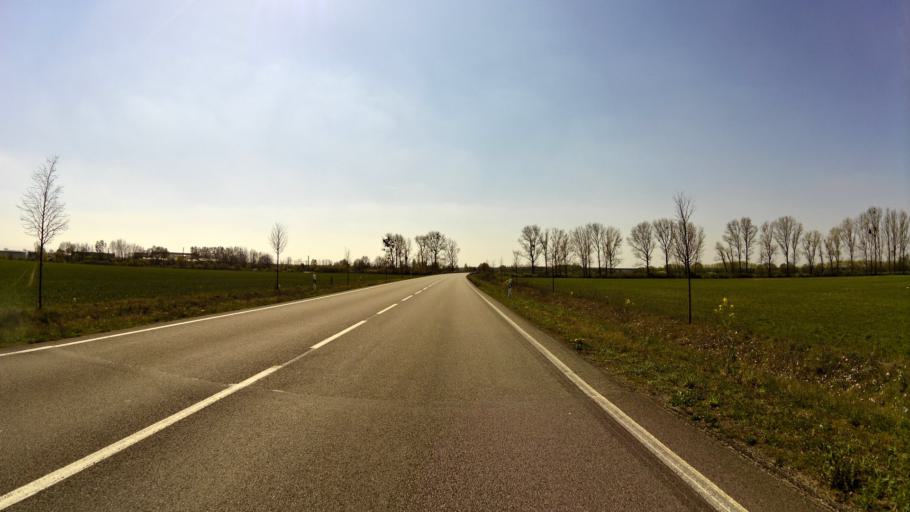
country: DE
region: Saxony-Anhalt
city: Oebisfelde
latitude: 52.4390
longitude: 10.9682
